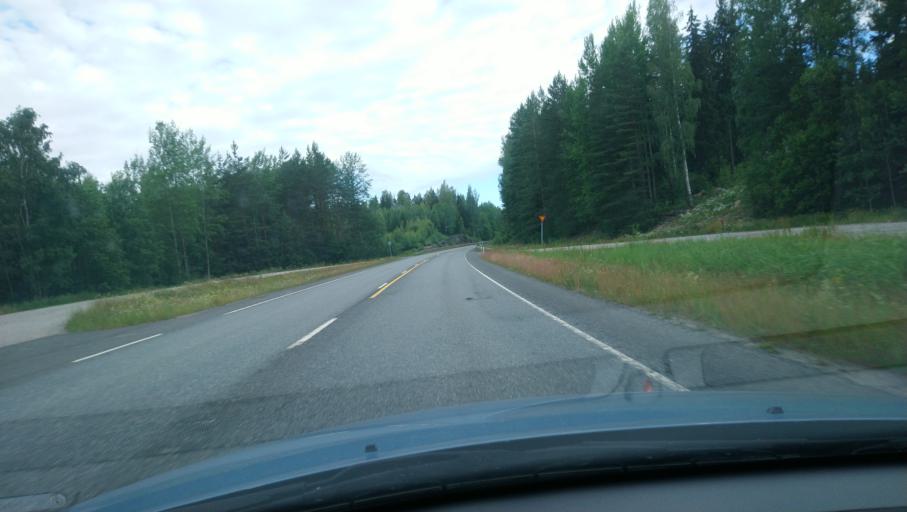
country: FI
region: Uusimaa
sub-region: Porvoo
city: Porvoo
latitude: 60.4312
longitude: 25.5757
